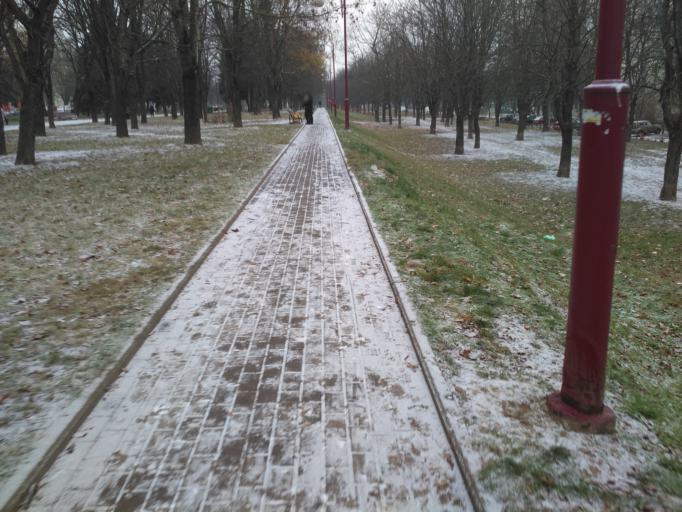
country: BY
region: Minsk
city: Novoye Medvezhino
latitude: 53.9122
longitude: 27.4879
